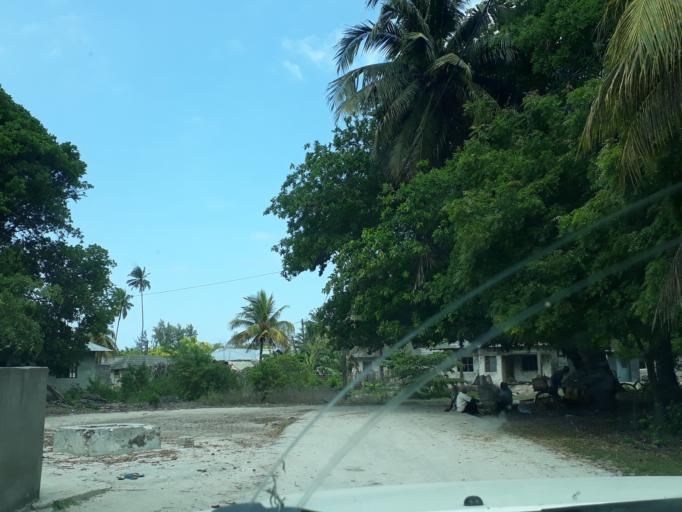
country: TZ
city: Kiwengwa
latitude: -6.0417
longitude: 39.4067
